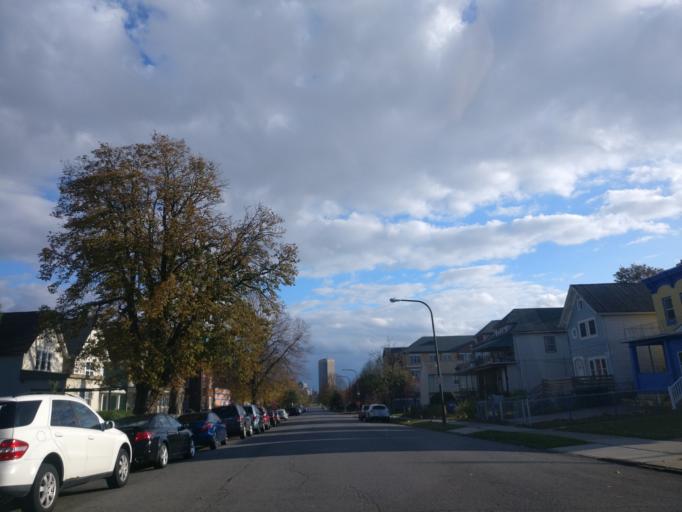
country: US
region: New York
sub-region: Erie County
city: Buffalo
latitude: 42.8962
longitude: -78.8907
